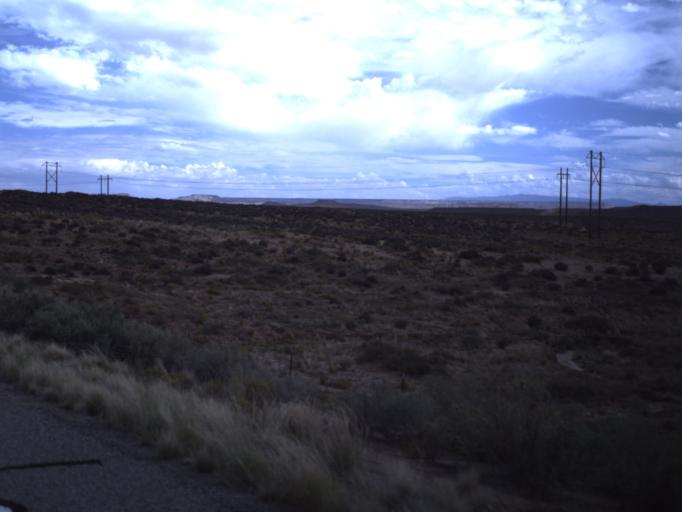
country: US
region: Utah
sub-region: San Juan County
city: Blanding
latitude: 37.3007
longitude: -109.4385
